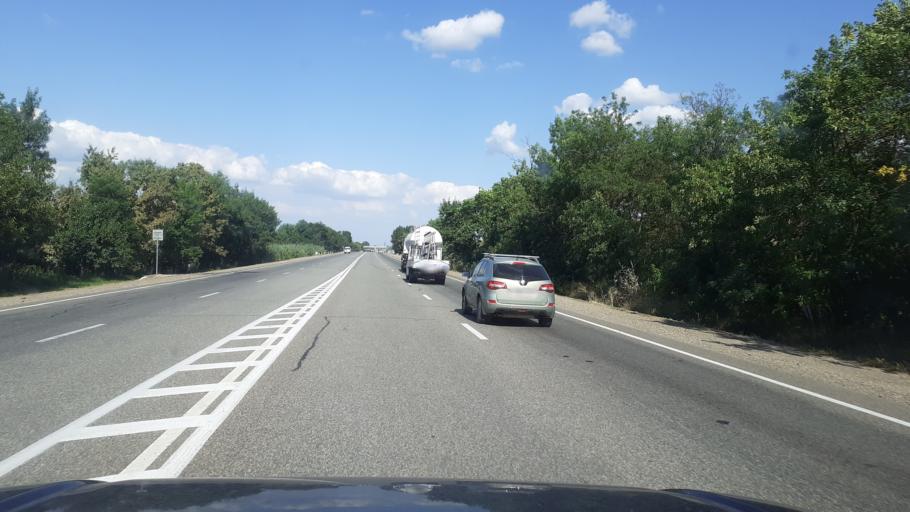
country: RU
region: Krasnodarskiy
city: Afipskiy
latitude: 44.8840
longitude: 38.7946
